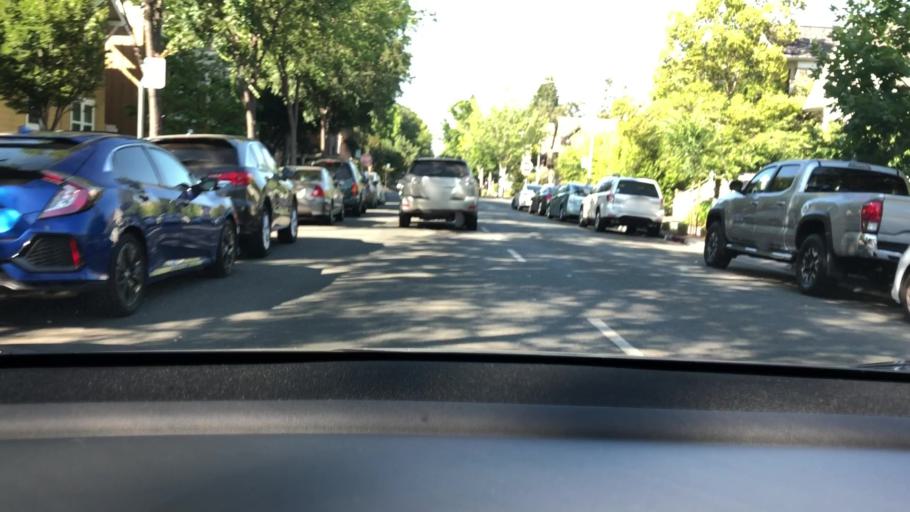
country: US
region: California
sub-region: Santa Clara County
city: Palo Alto
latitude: 37.4422
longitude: -122.1572
